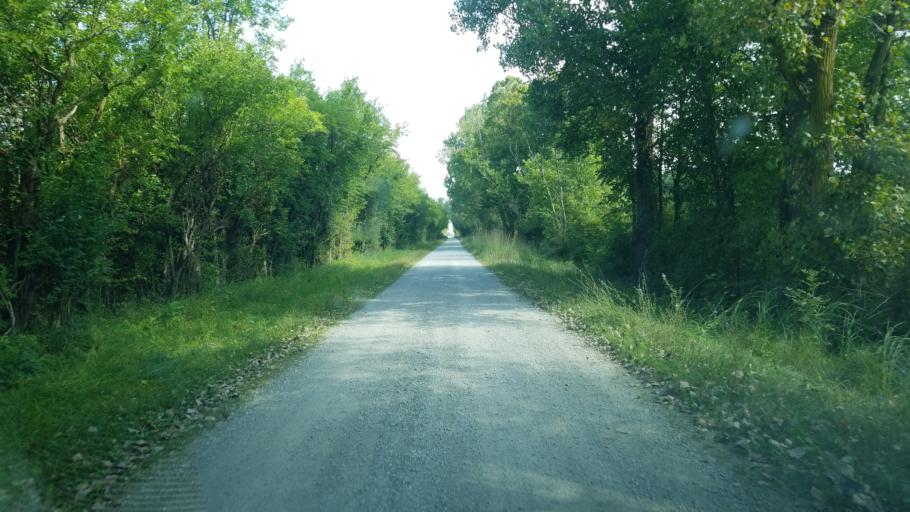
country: US
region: Ohio
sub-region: Wyandot County
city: Upper Sandusky
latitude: 40.6991
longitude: -83.3239
